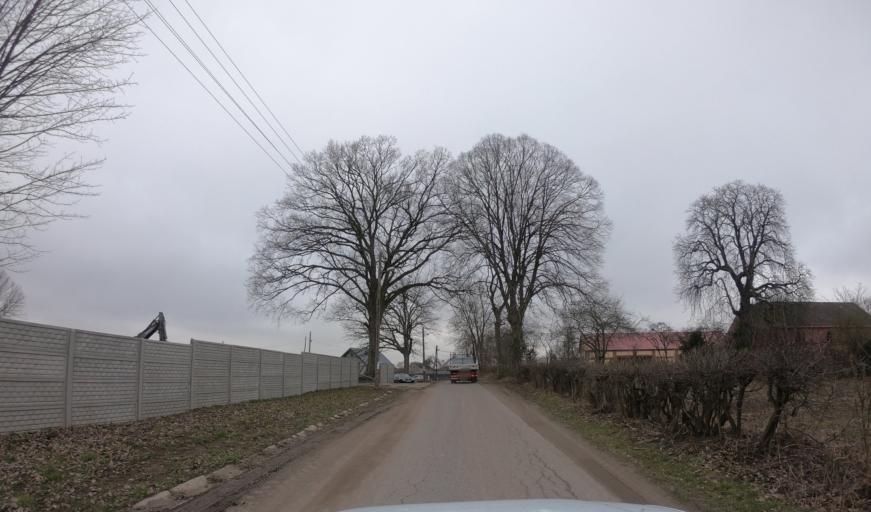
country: PL
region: West Pomeranian Voivodeship
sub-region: Powiat gryficki
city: Ploty
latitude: 53.8471
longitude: 15.2822
